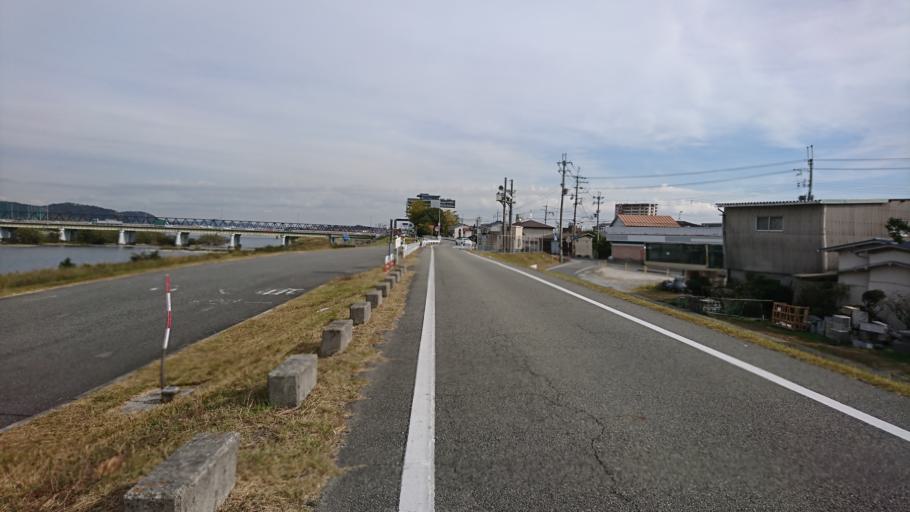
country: JP
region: Hyogo
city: Kakogawacho-honmachi
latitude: 34.7704
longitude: 134.8261
